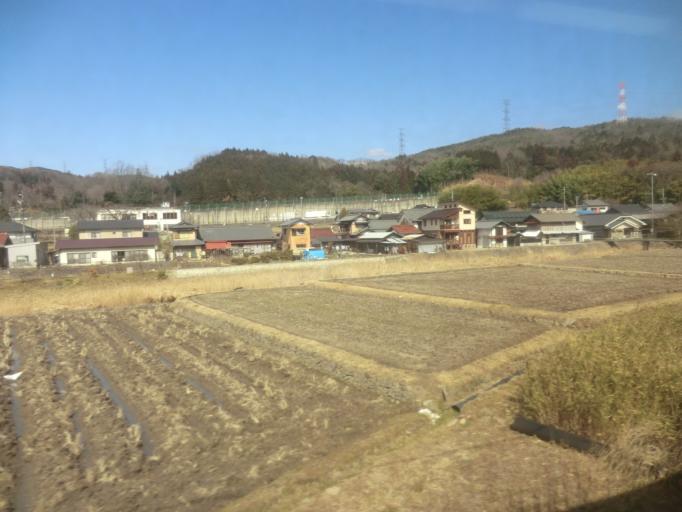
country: JP
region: Gifu
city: Mizunami
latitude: 35.4168
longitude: 137.3179
